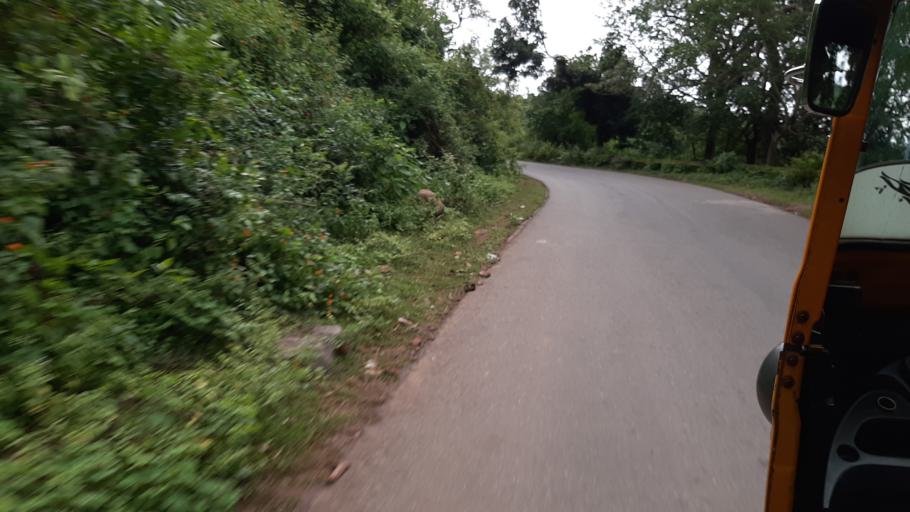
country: IN
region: Andhra Pradesh
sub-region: Vizianagaram District
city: Salur
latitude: 18.2447
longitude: 83.0256
